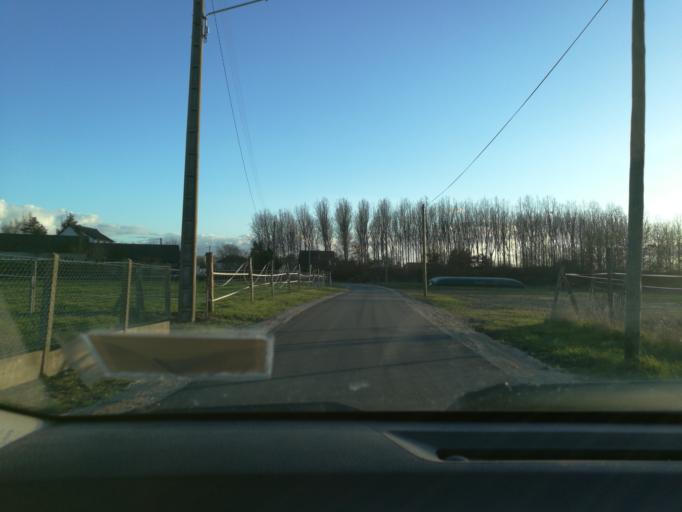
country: FR
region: Centre
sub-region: Departement du Loiret
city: Semoy
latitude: 47.9367
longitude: 1.9653
